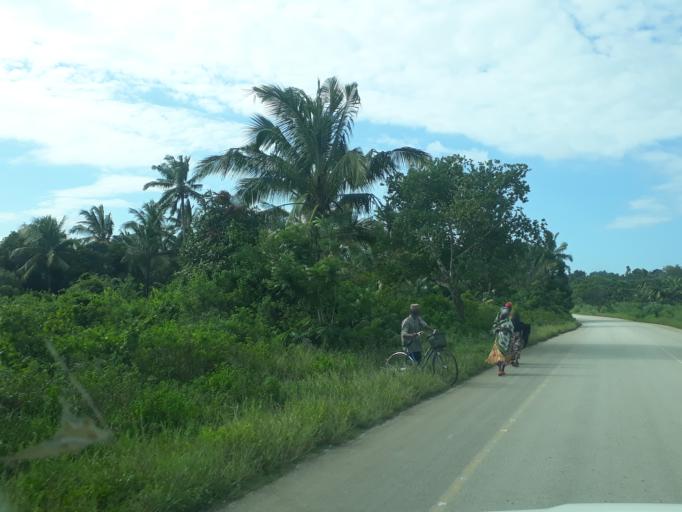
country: TZ
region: Zanzibar North
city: Kijini
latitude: -5.8357
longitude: 39.2892
